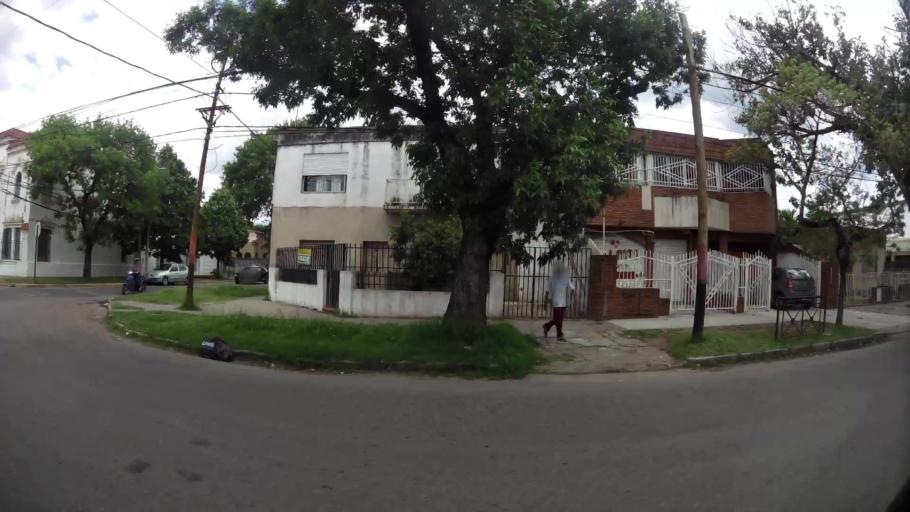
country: AR
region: Santa Fe
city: Gobernador Galvez
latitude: -32.9999
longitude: -60.6453
